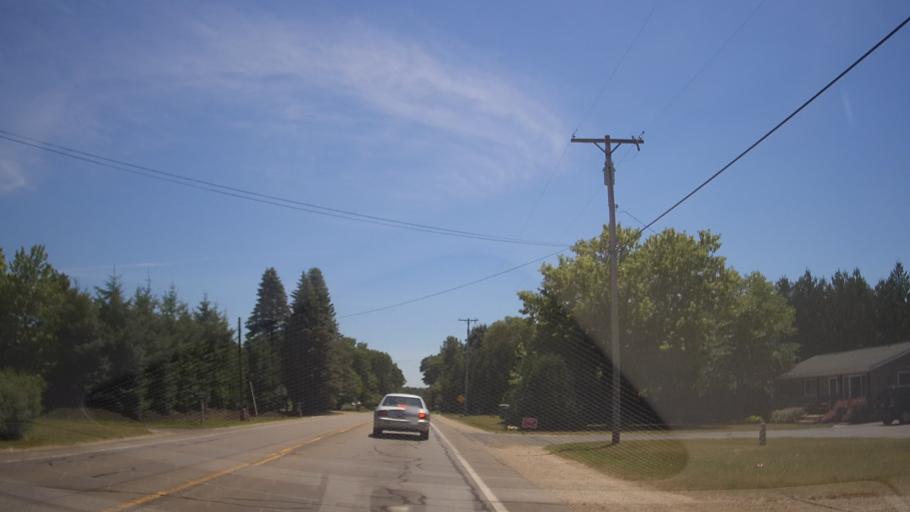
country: US
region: Michigan
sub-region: Grand Traverse County
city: Traverse City
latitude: 44.6934
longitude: -85.6911
